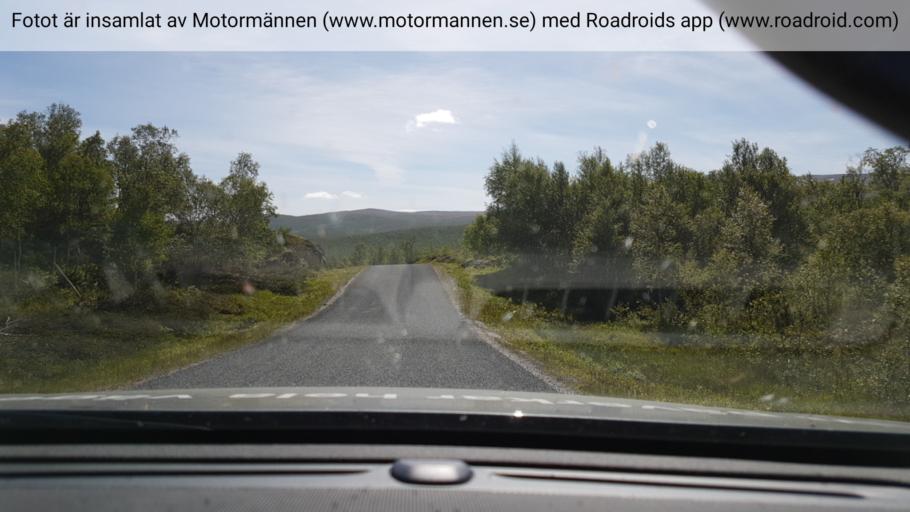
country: NO
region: Nordland
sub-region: Hattfjelldal
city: Hattfjelldal
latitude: 65.4176
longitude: 14.6846
